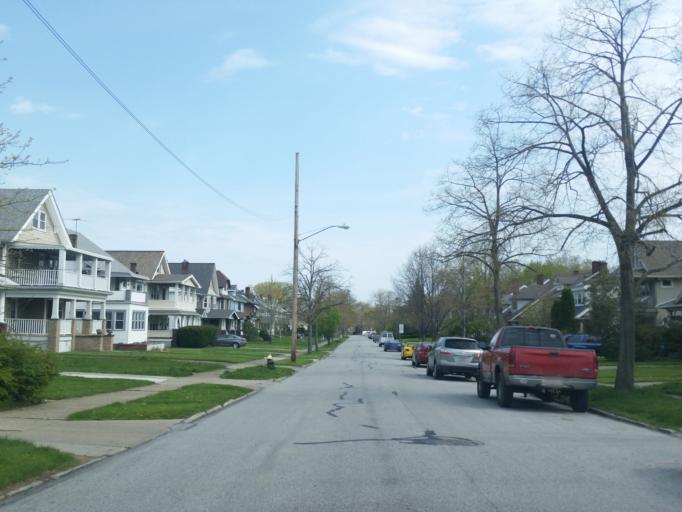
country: US
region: Ohio
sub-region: Cuyahoga County
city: Lakewood
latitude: 41.4781
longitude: -81.7829
